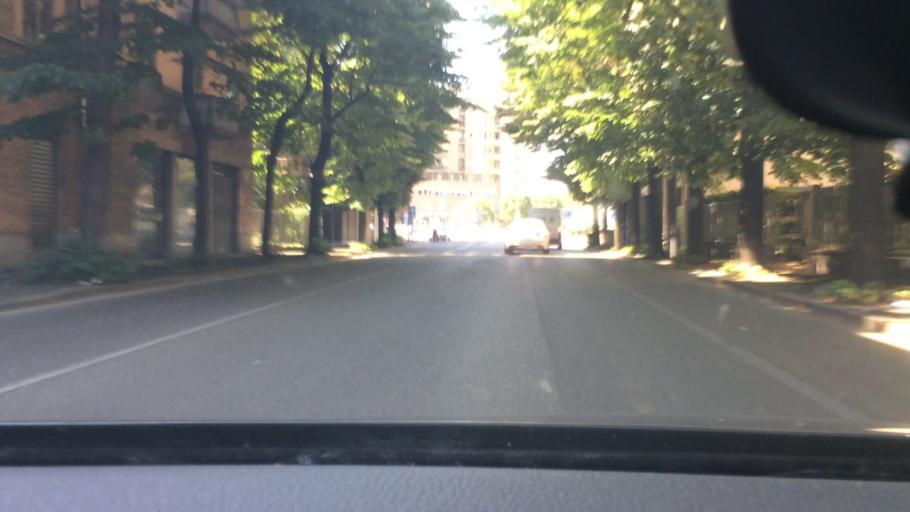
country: IT
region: Emilia-Romagna
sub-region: Provincia di Piacenza
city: Piacenza
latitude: 45.0553
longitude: 9.6772
